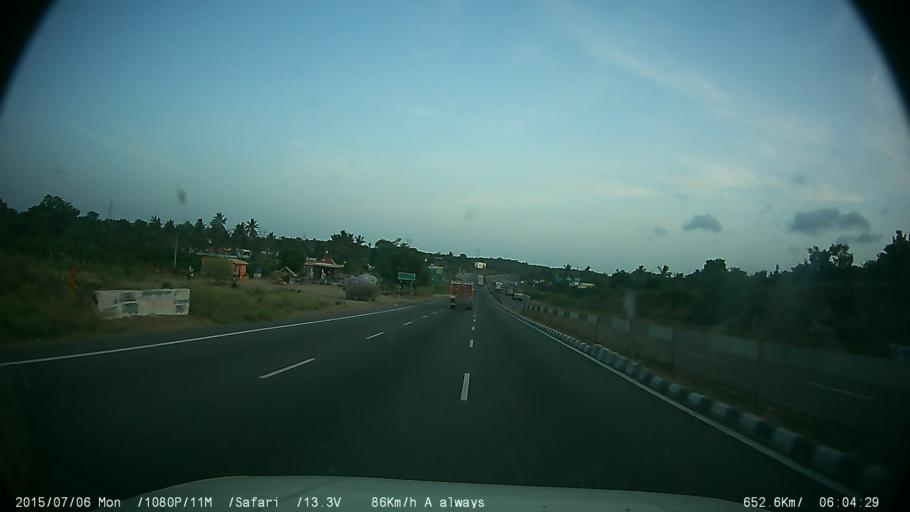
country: IN
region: Tamil Nadu
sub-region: Krishnagiri
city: Krishnagiri
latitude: 12.6150
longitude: 78.0874
